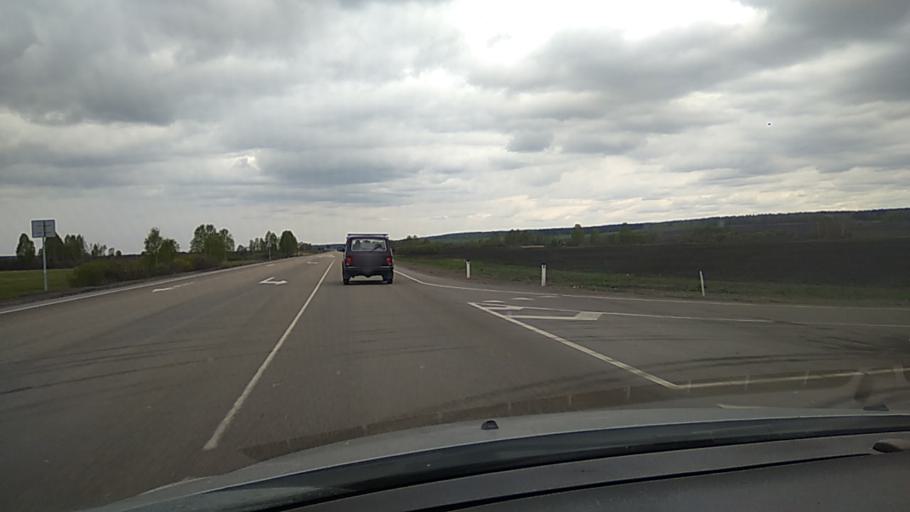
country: RU
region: Kurgan
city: Kataysk
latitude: 56.2981
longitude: 62.4492
